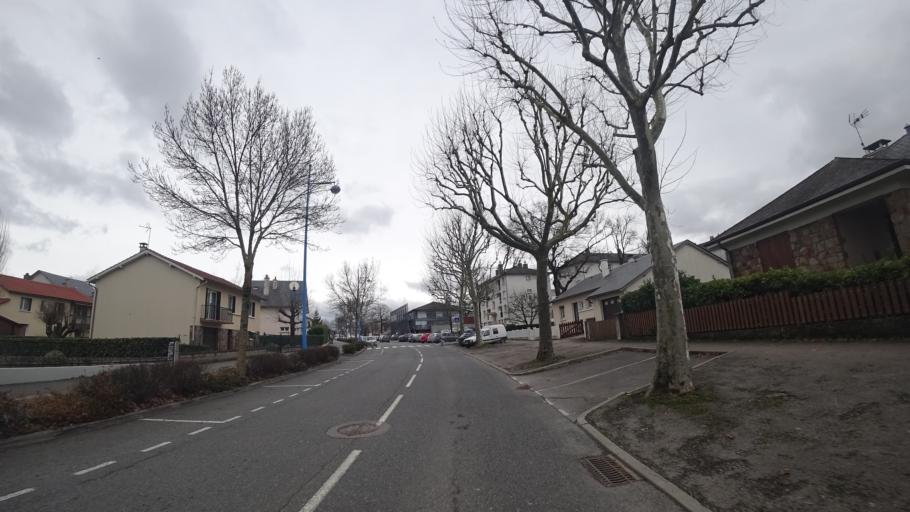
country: FR
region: Midi-Pyrenees
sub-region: Departement de l'Aveyron
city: Rodez
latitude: 44.3677
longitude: 2.5924
